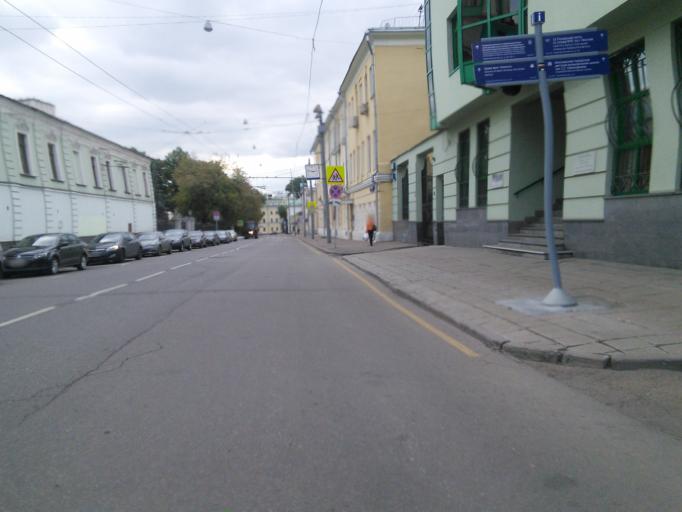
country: RU
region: Moscow
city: Lefortovo
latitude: 55.7730
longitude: 37.6744
